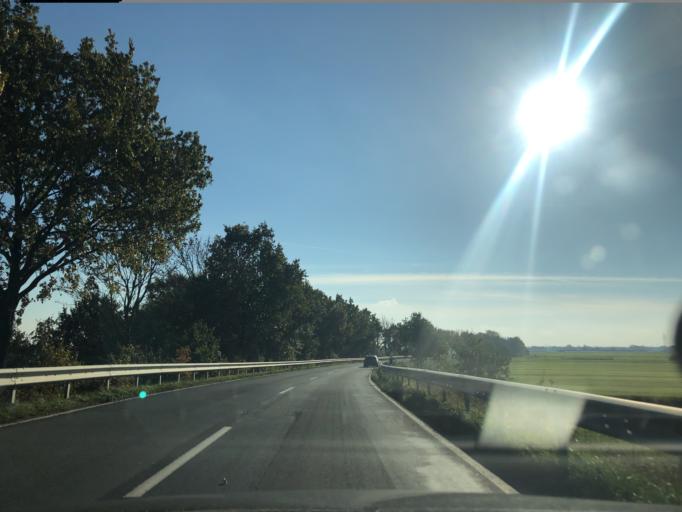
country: DE
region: Lower Saxony
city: Lemwerder
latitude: 53.1727
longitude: 8.5578
